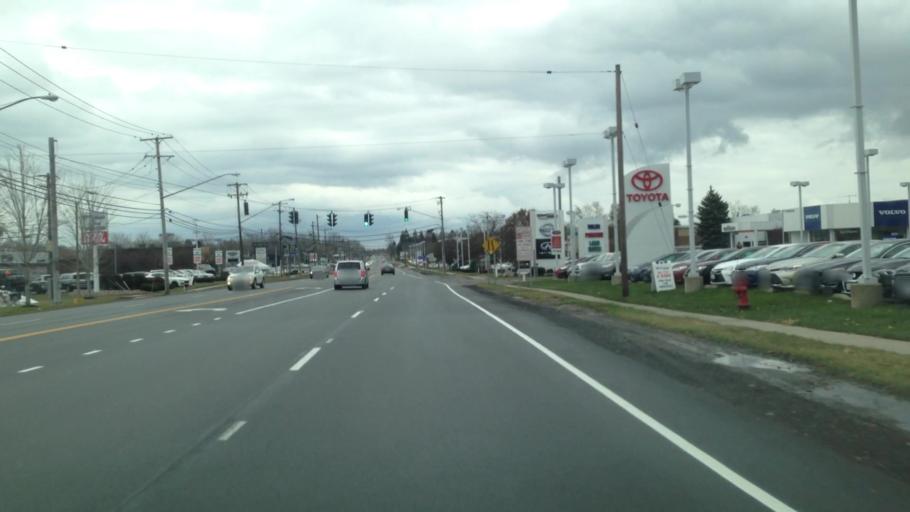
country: US
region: New York
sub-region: Erie County
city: Harris Hill
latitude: 42.9651
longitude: -78.6932
